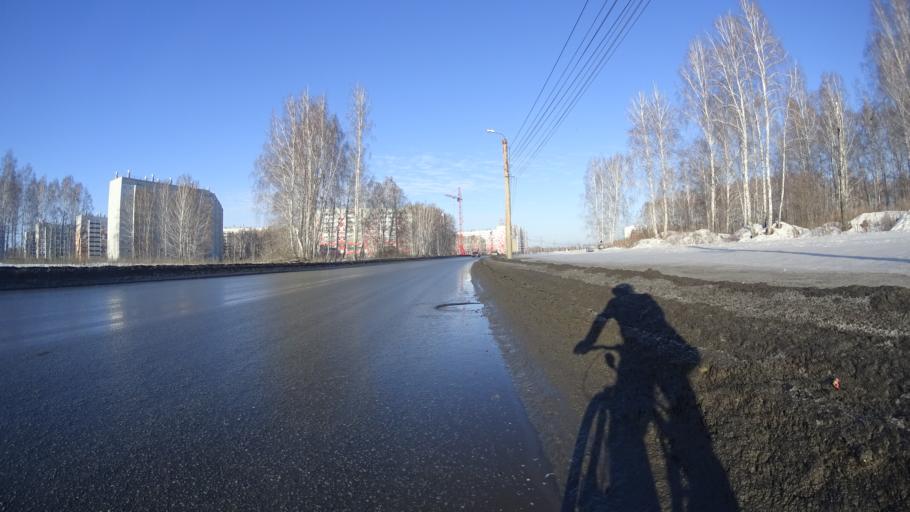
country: RU
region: Chelyabinsk
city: Roshchino
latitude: 55.2147
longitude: 61.2854
